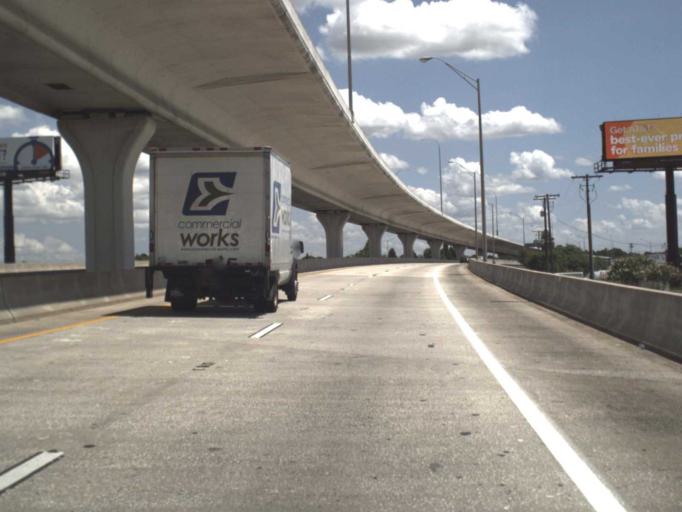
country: US
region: Florida
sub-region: Hillsborough County
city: Palm River-Clair Mel
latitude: 27.9504
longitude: -82.3717
